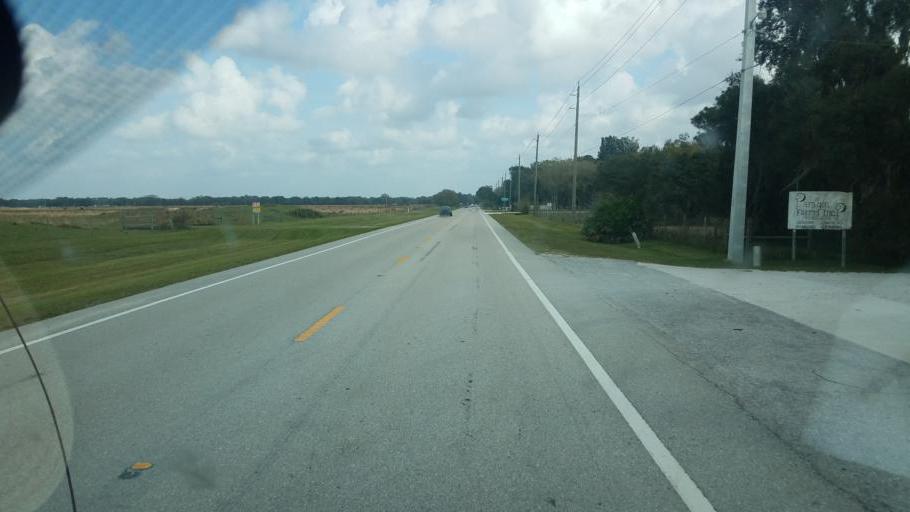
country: US
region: Florida
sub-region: Sarasota County
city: Lake Sarasota
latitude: 27.3344
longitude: -82.2793
